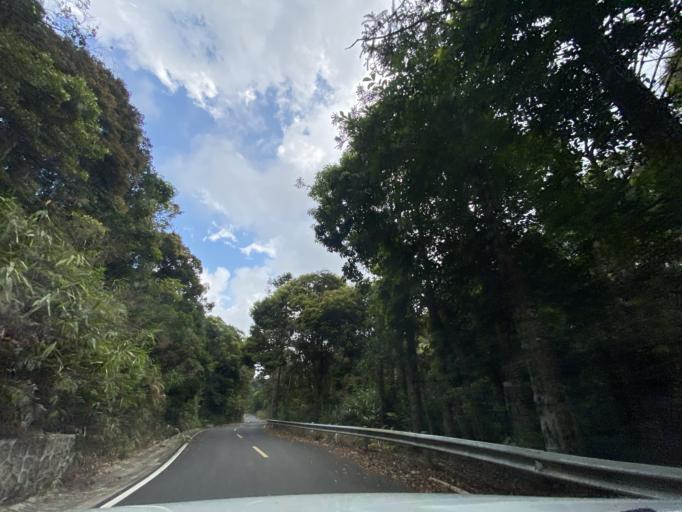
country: CN
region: Hainan
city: Diaoluoshan
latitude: 18.7221
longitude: 109.8699
